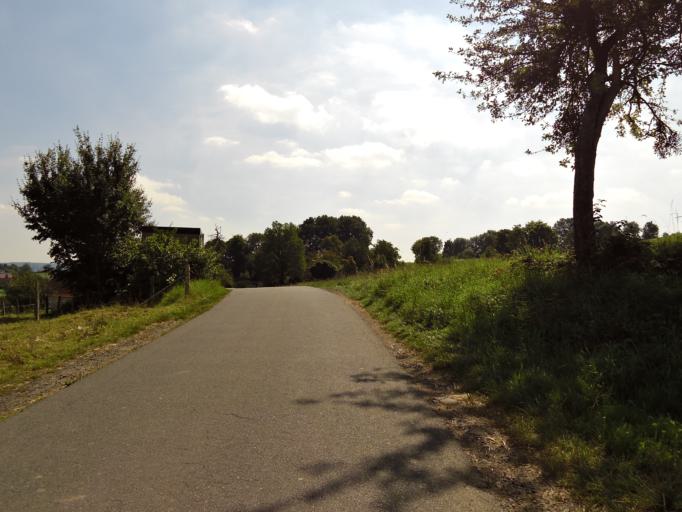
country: DE
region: Hesse
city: Reichelsheim
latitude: 49.7207
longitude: 8.8003
